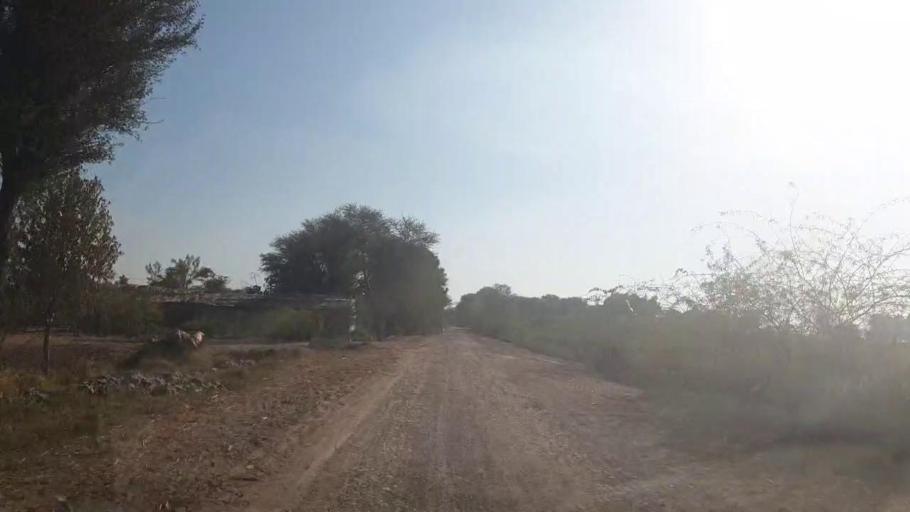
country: PK
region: Sindh
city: Mirwah Gorchani
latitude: 25.4236
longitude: 69.1646
